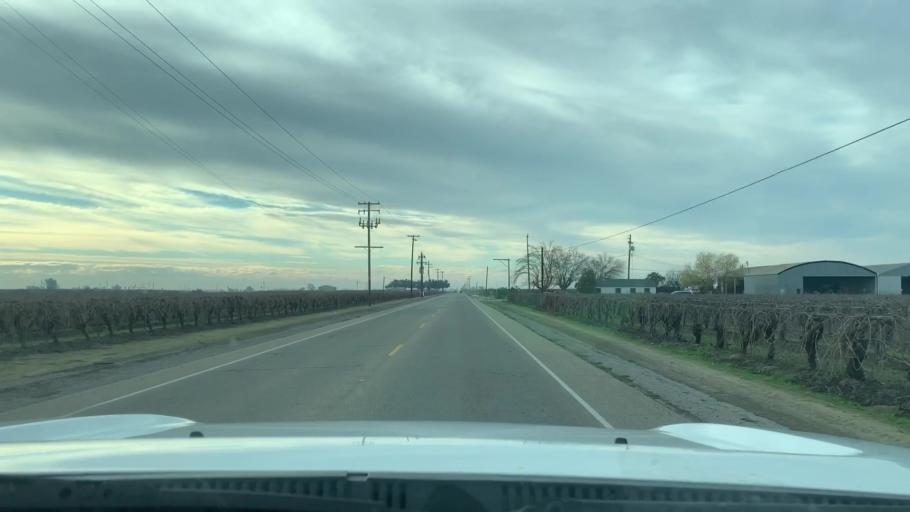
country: US
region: California
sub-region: Fresno County
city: Fowler
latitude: 36.6055
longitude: -119.6922
